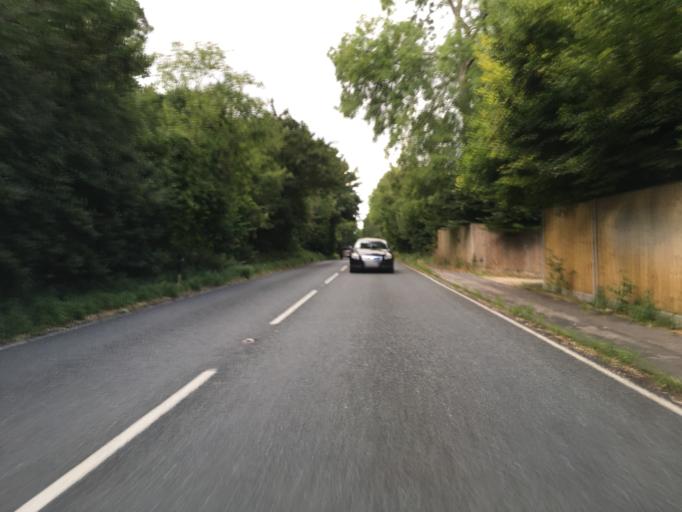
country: GB
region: England
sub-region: Hampshire
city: Kings Worthy
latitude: 51.1519
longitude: -1.2419
